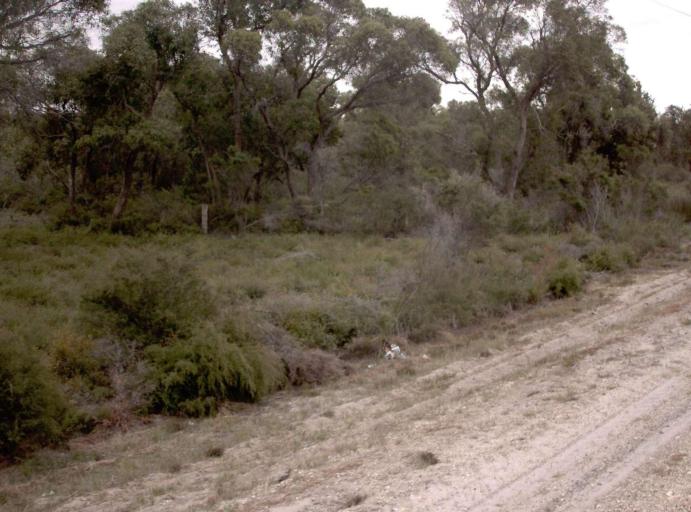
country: AU
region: Victoria
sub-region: Wellington
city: Sale
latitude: -38.1750
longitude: 147.3815
